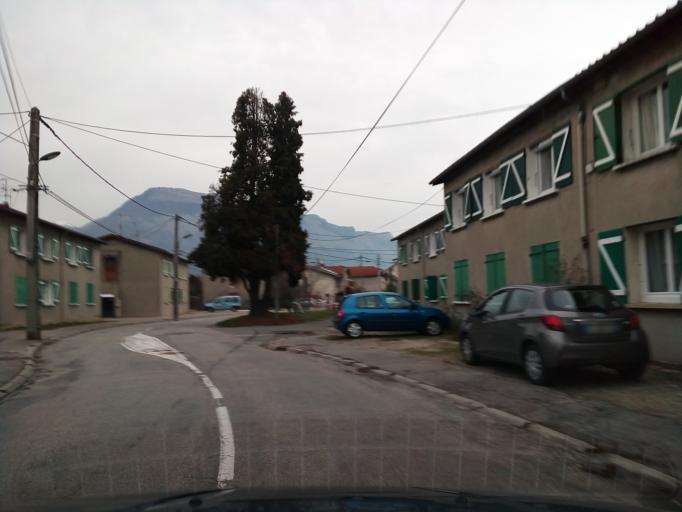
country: FR
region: Rhone-Alpes
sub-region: Departement de l'Isere
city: Saint-Martin-d'Heres
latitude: 45.1818
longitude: 5.7631
